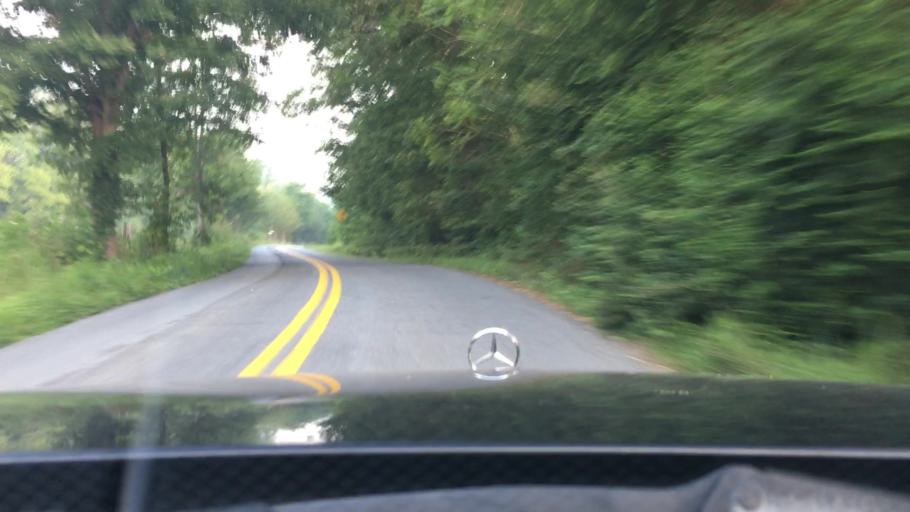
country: US
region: Virginia
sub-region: Campbell County
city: Timberlake
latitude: 37.2783
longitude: -79.2687
